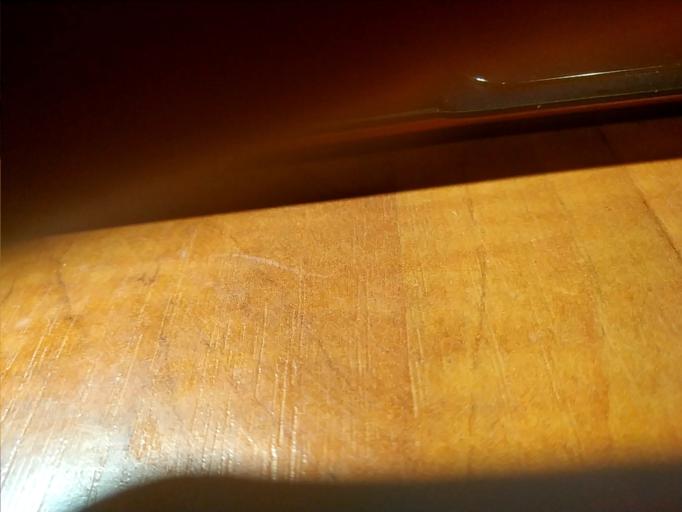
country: RU
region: Tverskaya
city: Ves'yegonsk
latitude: 58.7193
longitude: 37.5439
